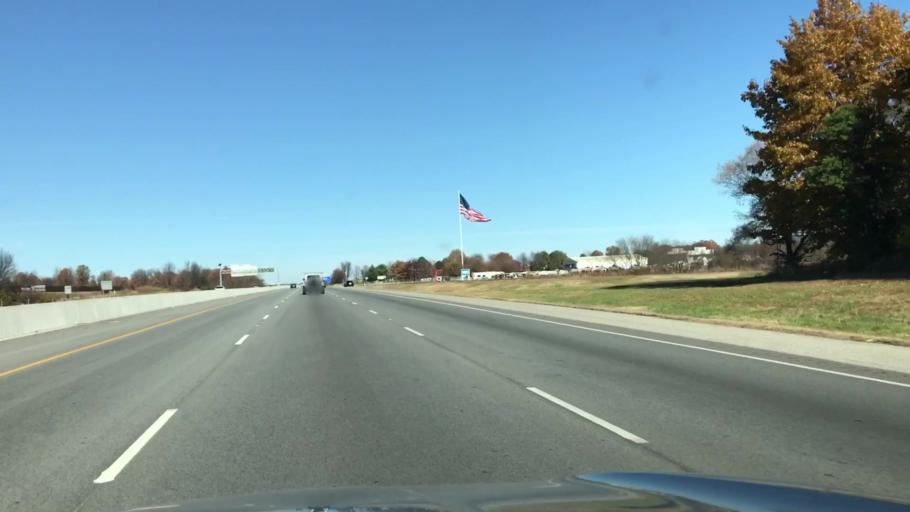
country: US
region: Arkansas
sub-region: Benton County
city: Lowell
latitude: 36.2568
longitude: -94.1501
